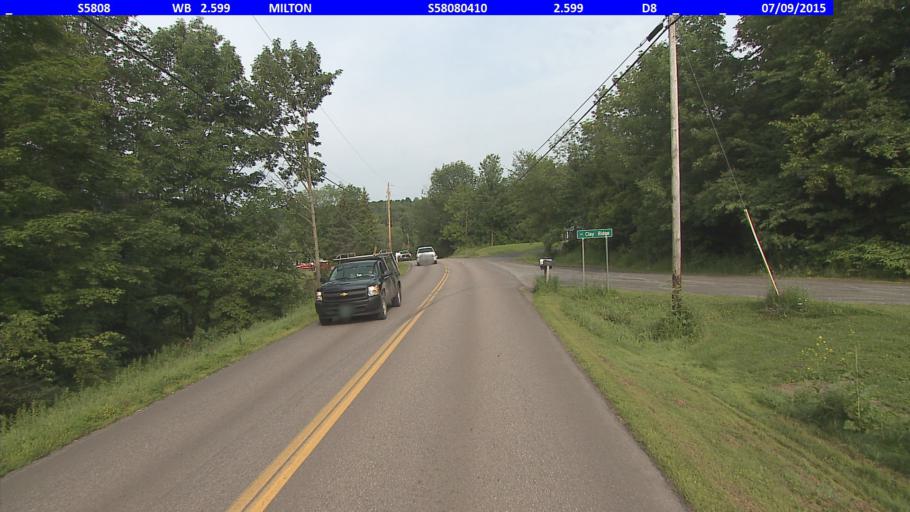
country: US
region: Vermont
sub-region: Chittenden County
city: Milton
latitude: 44.6442
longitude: -73.0666
